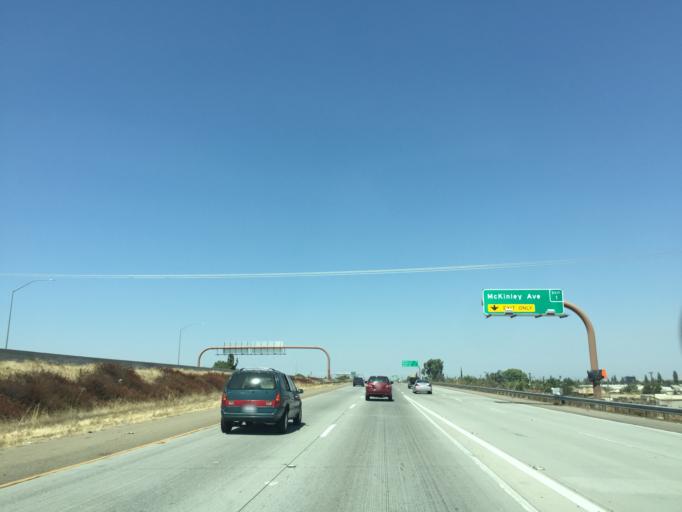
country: US
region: California
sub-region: Fresno County
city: Fresno
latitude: 36.7590
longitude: -119.7491
